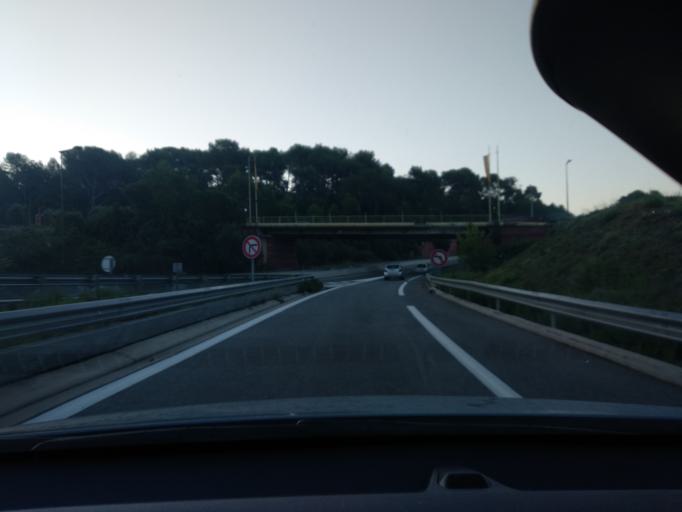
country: FR
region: Provence-Alpes-Cote d'Azur
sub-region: Departement des Alpes-Maritimes
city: Grasse
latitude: 43.6416
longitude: 6.9350
